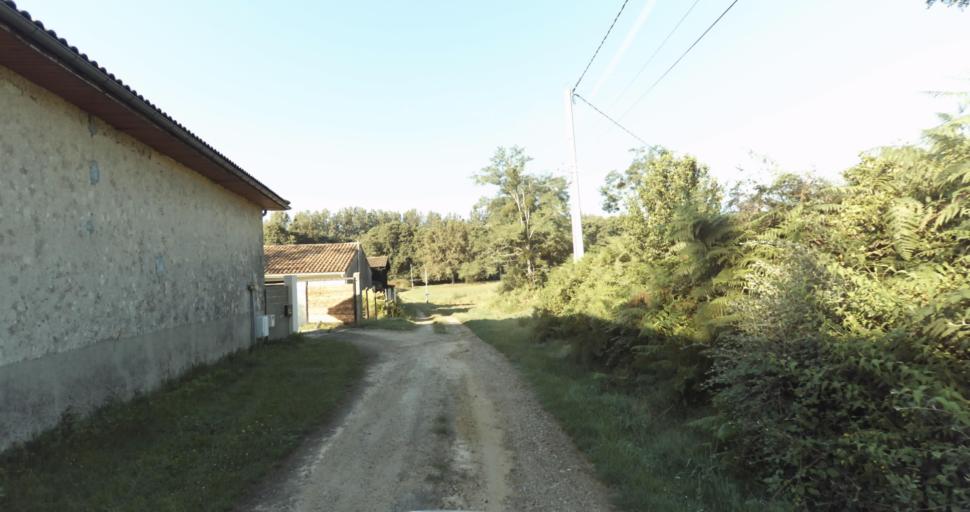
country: FR
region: Aquitaine
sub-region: Departement de la Gironde
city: Bazas
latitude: 44.4077
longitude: -0.2145
